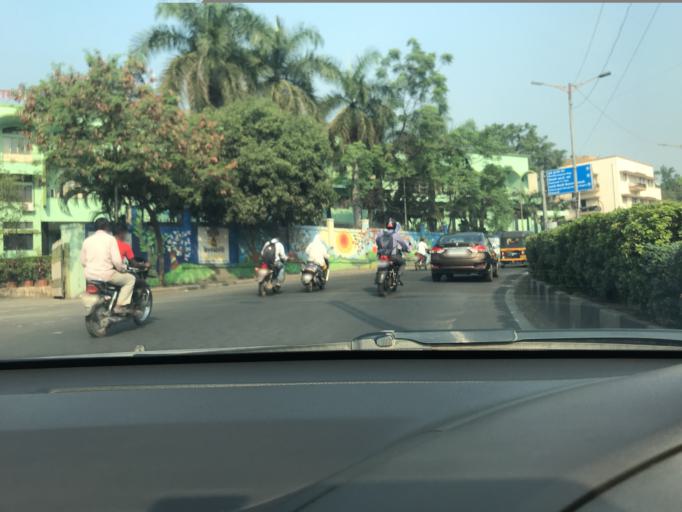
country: IN
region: Maharashtra
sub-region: Pune Division
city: Shivaji Nagar
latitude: 18.5206
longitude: 73.8292
